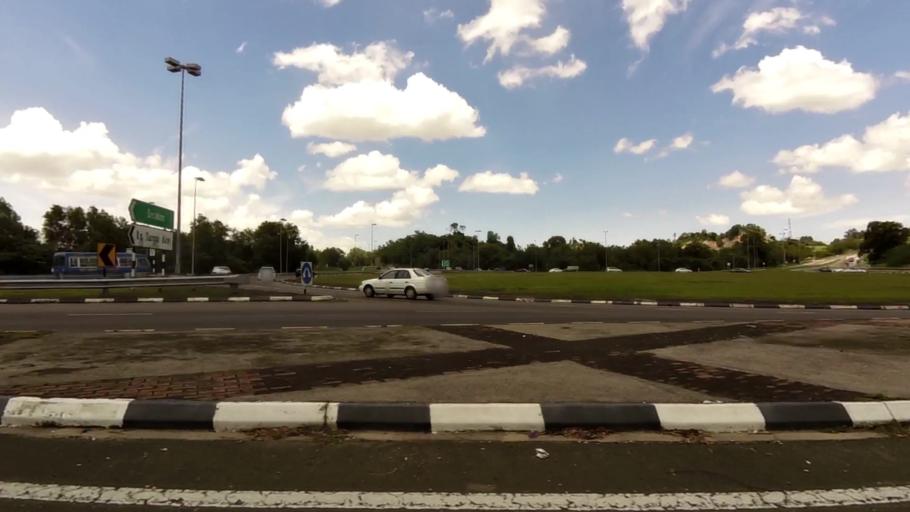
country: BN
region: Brunei and Muara
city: Bandar Seri Begawan
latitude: 4.9326
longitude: 114.9745
